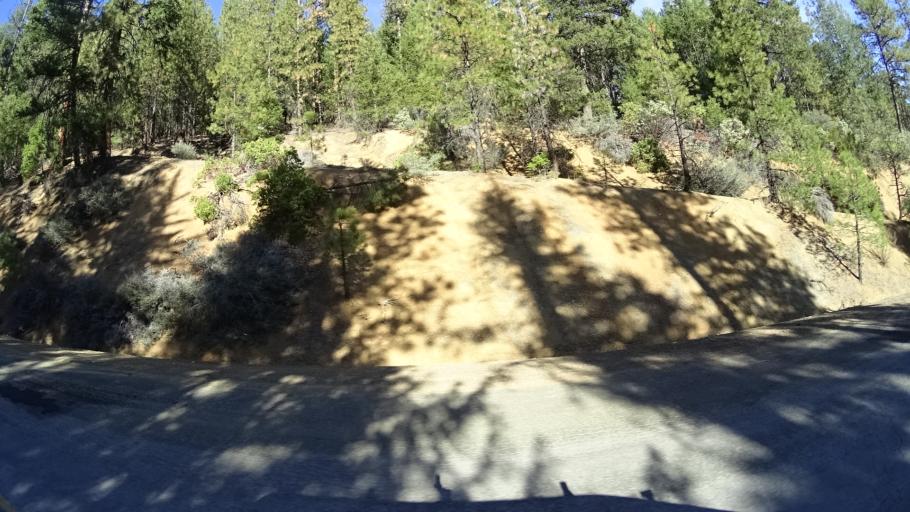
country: US
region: California
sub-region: Siskiyou County
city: Yreka
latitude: 41.7306
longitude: -122.7259
